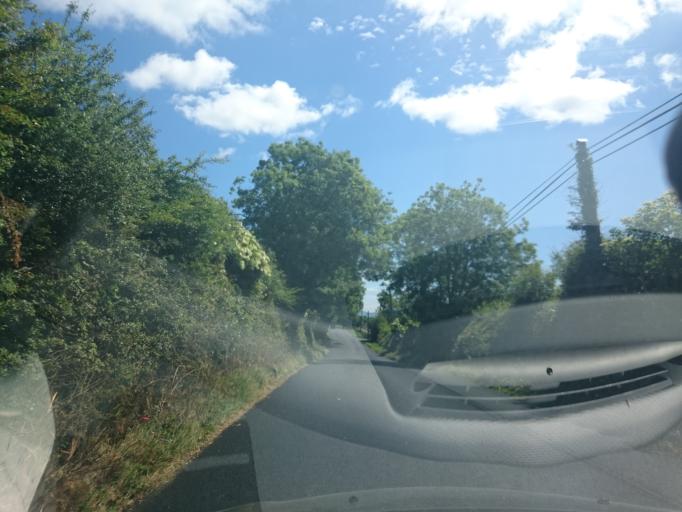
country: IE
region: Leinster
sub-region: Kilkenny
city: Thomastown
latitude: 52.6462
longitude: -7.1222
